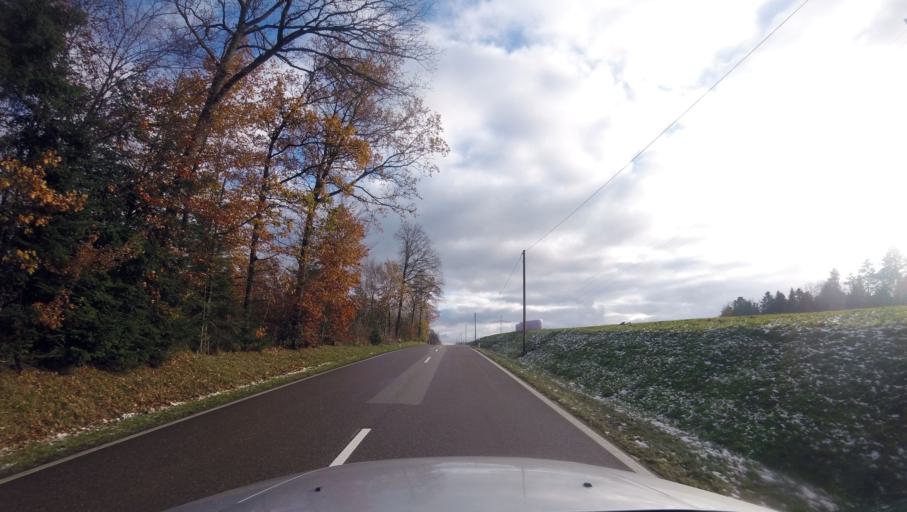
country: DE
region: Baden-Wuerttemberg
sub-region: Regierungsbezirk Stuttgart
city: Gschwend
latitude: 48.9082
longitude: 9.7457
